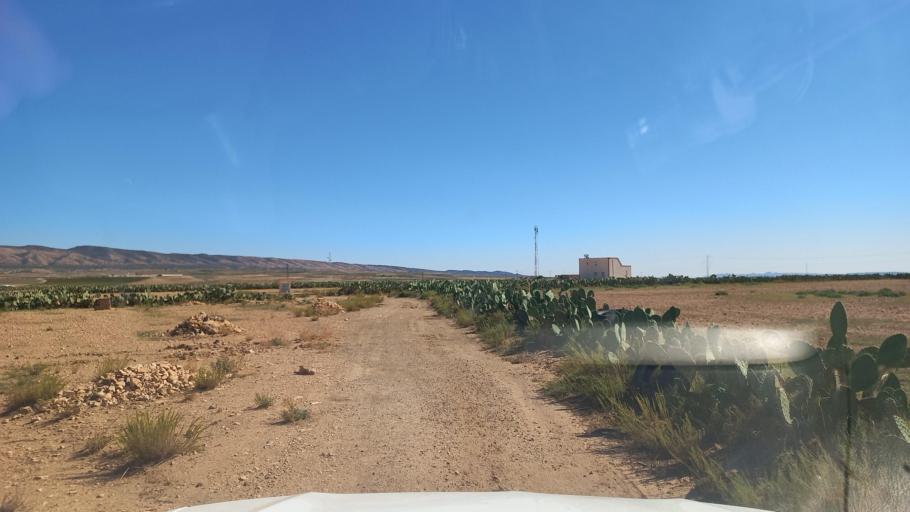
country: TN
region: Al Qasrayn
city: Sbiba
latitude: 35.3833
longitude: 9.0944
